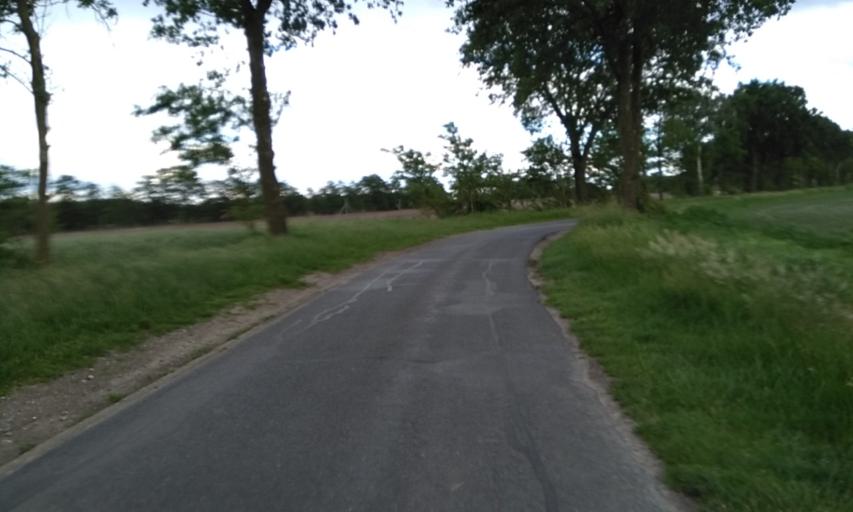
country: DE
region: Lower Saxony
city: Regesbostel
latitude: 53.3895
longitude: 9.6439
